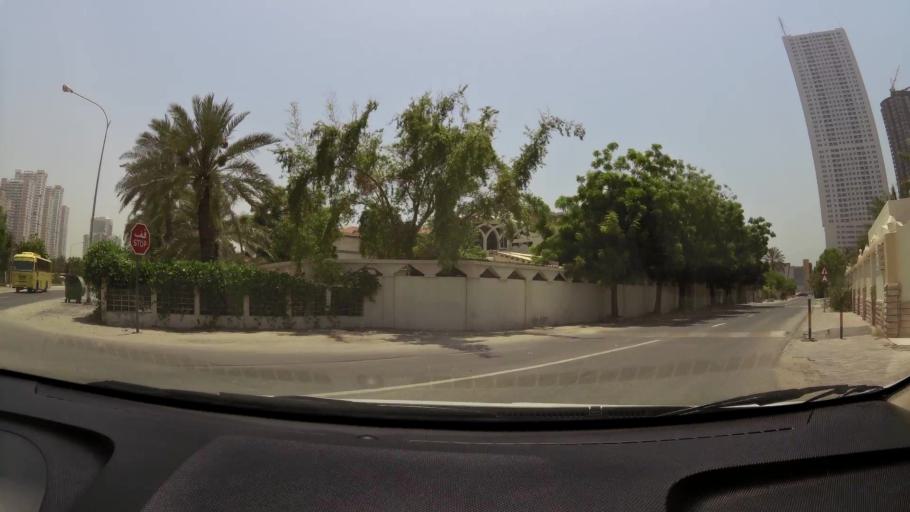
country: AE
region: Ajman
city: Ajman
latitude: 25.4016
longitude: 55.4325
